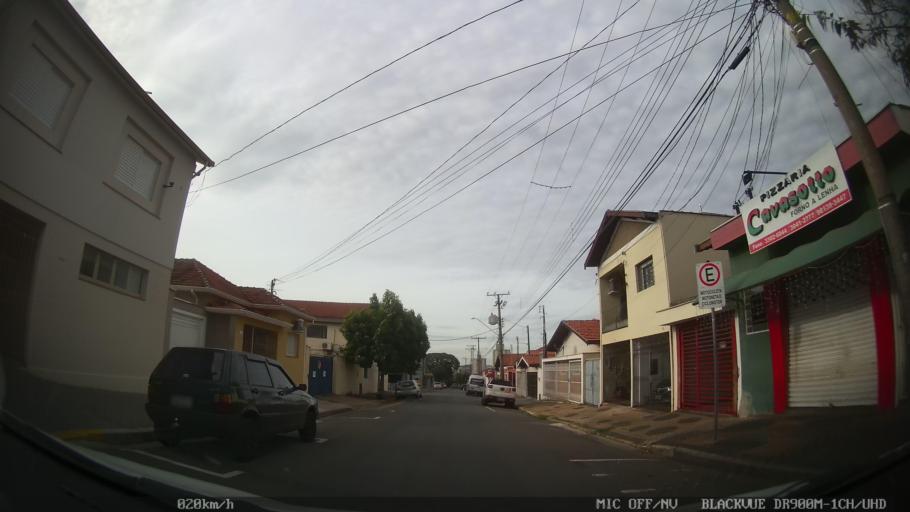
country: BR
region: Sao Paulo
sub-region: Piracicaba
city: Piracicaba
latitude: -22.7317
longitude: -47.6345
